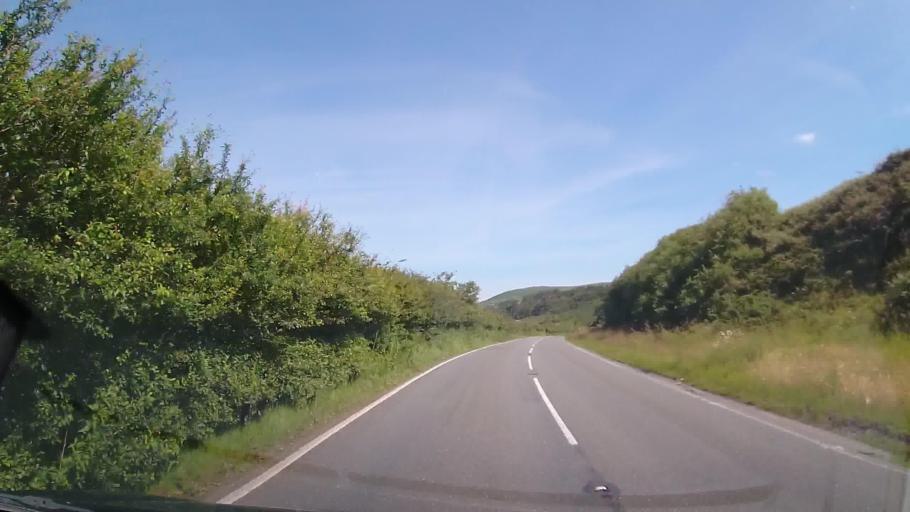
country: GB
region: Wales
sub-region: Gwynedd
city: Tywyn
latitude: 52.5568
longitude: -4.0723
